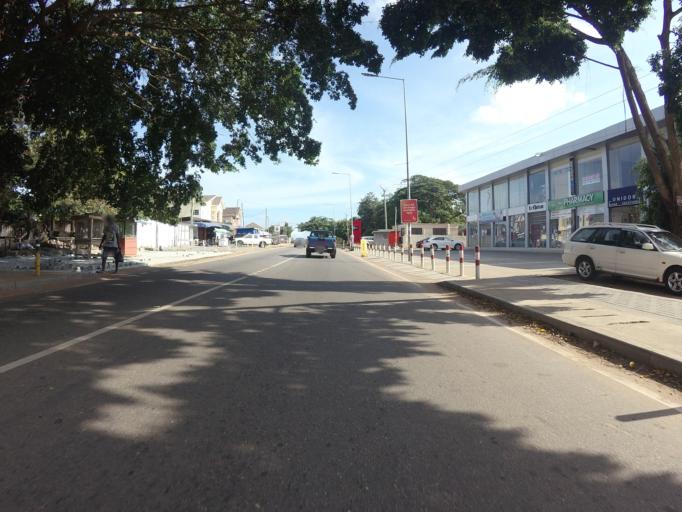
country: GH
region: Greater Accra
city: Medina Estates
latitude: 5.6400
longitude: -0.1620
